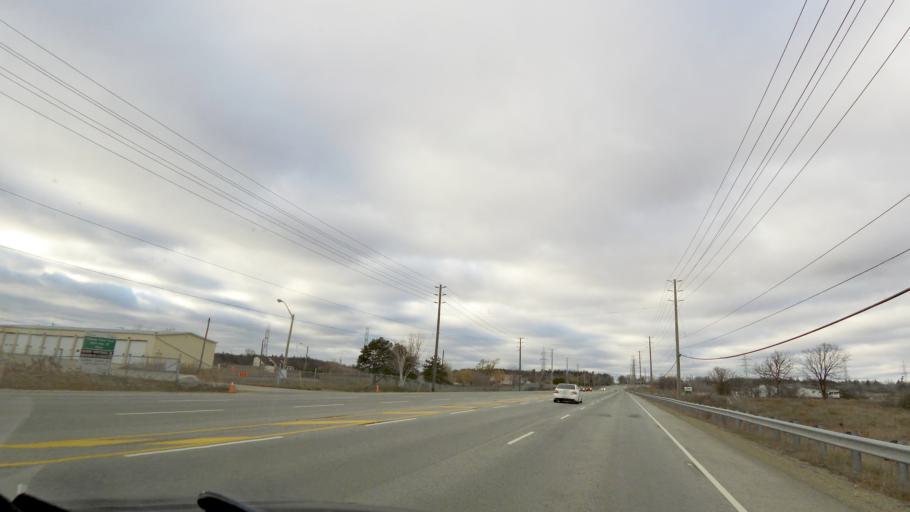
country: CA
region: Ontario
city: Burlington
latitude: 43.4500
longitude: -79.7961
